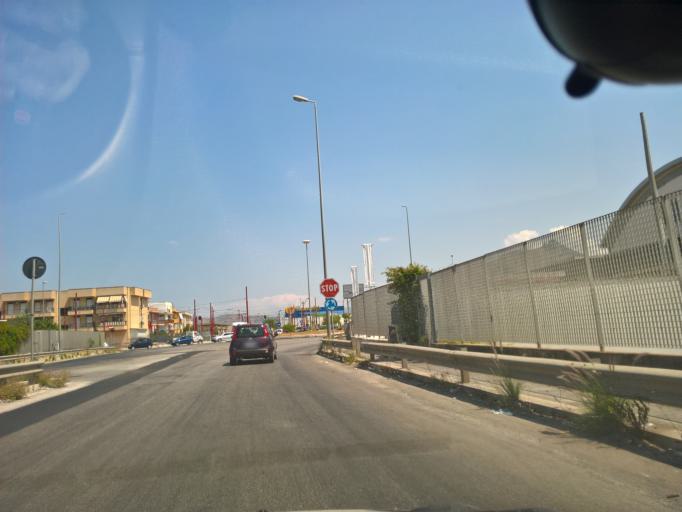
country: IT
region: Sicily
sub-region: Palermo
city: Ciaculli
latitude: 38.0919
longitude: 13.4090
